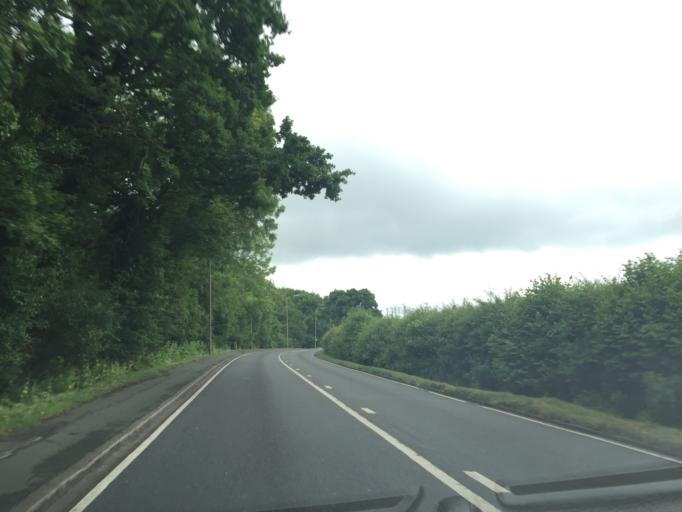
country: GB
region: England
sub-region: Essex
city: Epping
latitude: 51.7120
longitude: 0.1252
